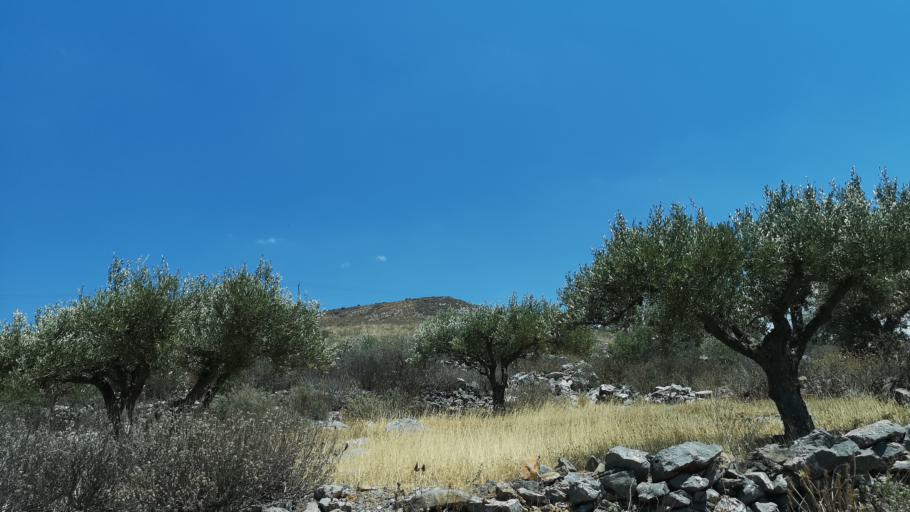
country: GR
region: Crete
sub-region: Nomos Lasithiou
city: Neapoli
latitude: 35.2543
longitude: 25.6389
